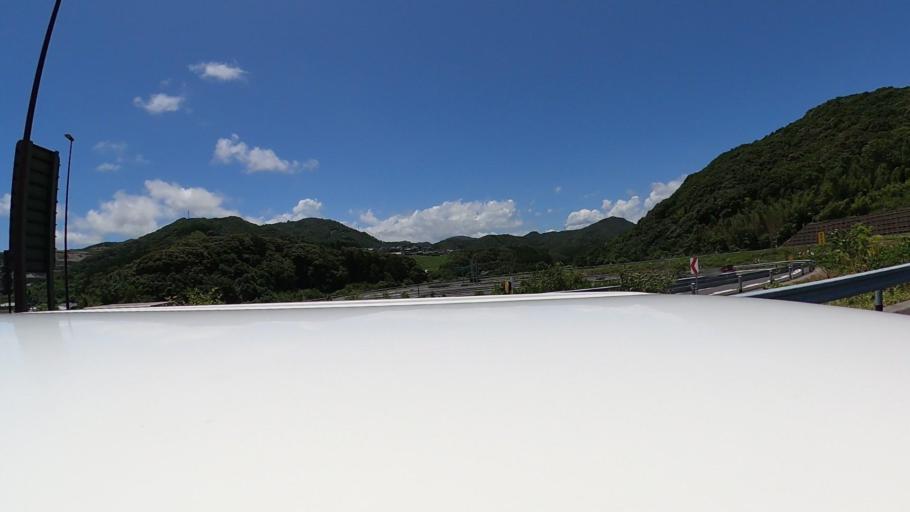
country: JP
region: Miyazaki
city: Nobeoka
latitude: 32.4006
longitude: 131.6167
